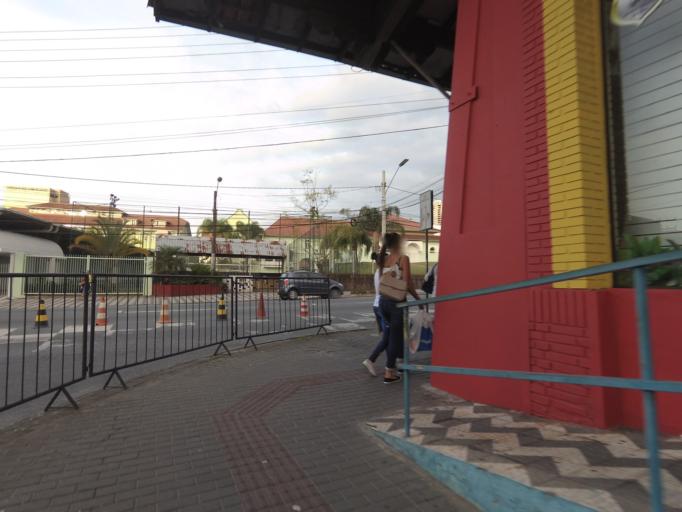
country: BR
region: Santa Catarina
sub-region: Blumenau
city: Blumenau
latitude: -26.9202
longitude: -49.0685
